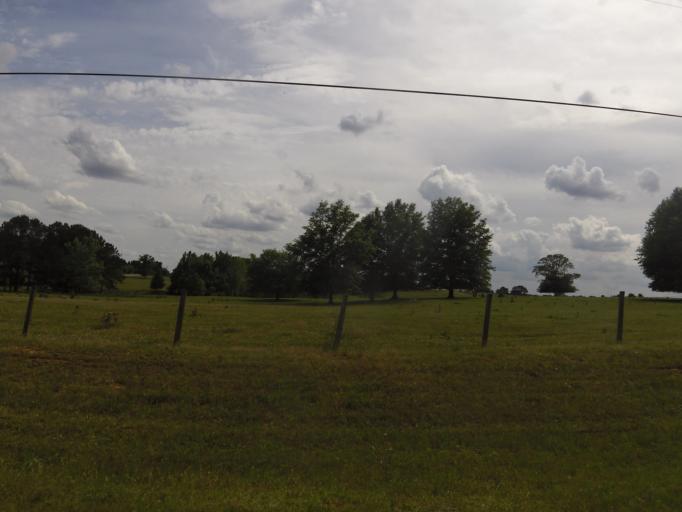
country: US
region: Georgia
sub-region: McDuffie County
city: Thomson
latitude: 33.5268
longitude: -82.4733
